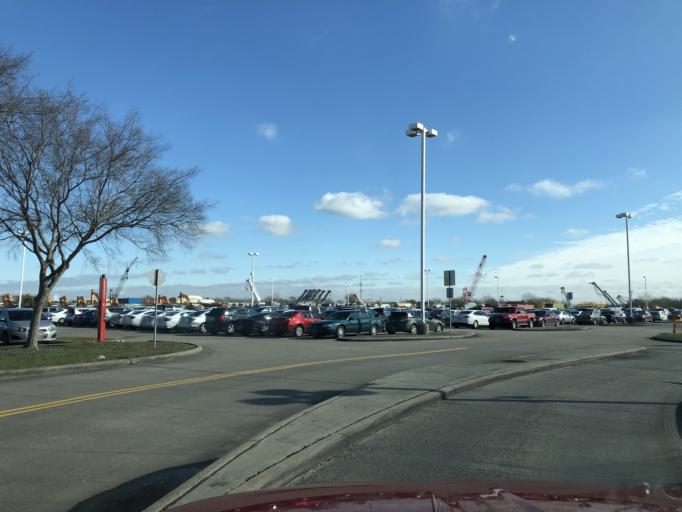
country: US
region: Texas
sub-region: Harris County
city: South Houston
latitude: 29.6640
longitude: -95.2557
